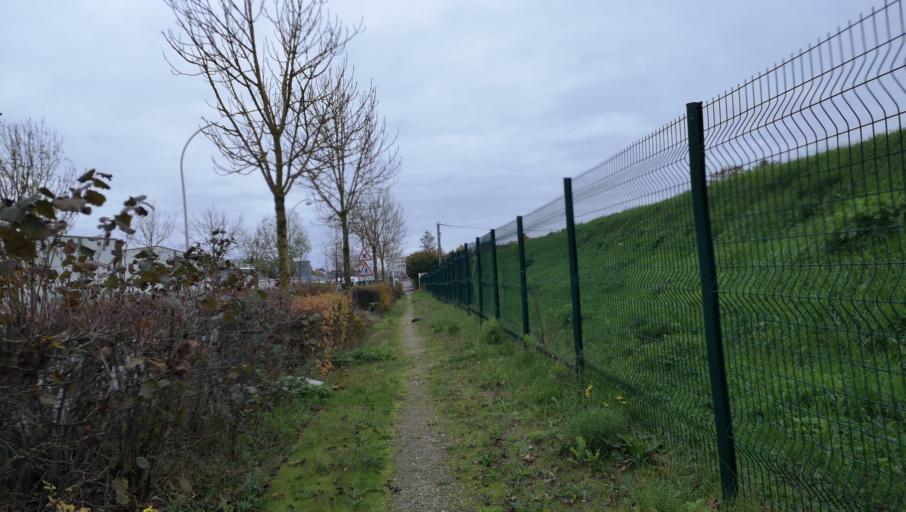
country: FR
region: Centre
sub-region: Departement du Loiret
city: Semoy
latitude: 47.9208
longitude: 1.9473
